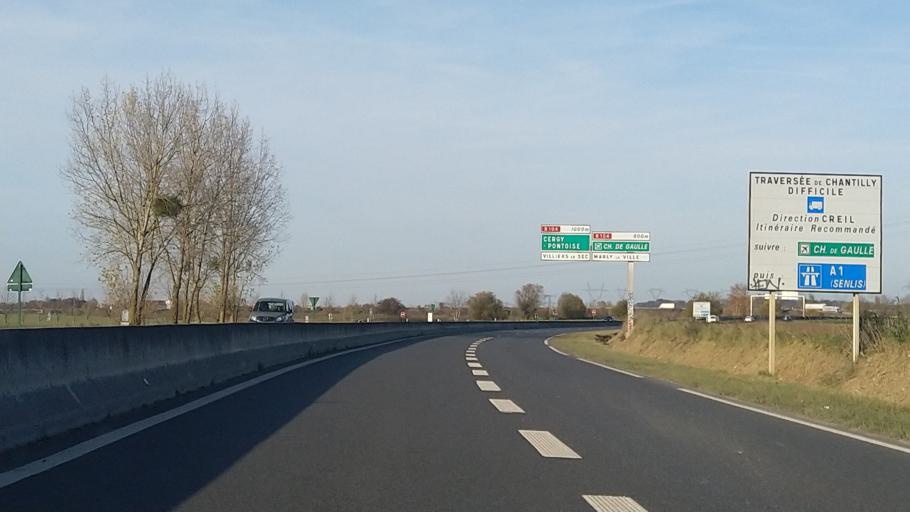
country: FR
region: Ile-de-France
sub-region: Departement du Val-d'Oise
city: Ecouen
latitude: 49.0562
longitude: 2.4022
